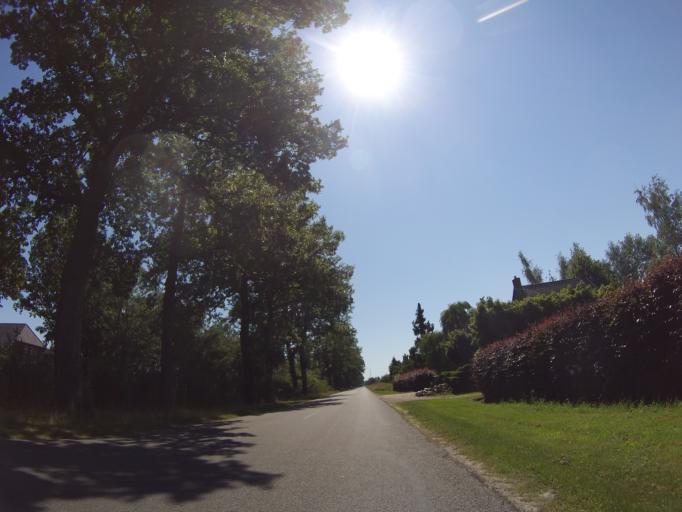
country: NL
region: Drenthe
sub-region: Gemeente Borger-Odoorn
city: Borger
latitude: 52.8500
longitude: 6.7722
